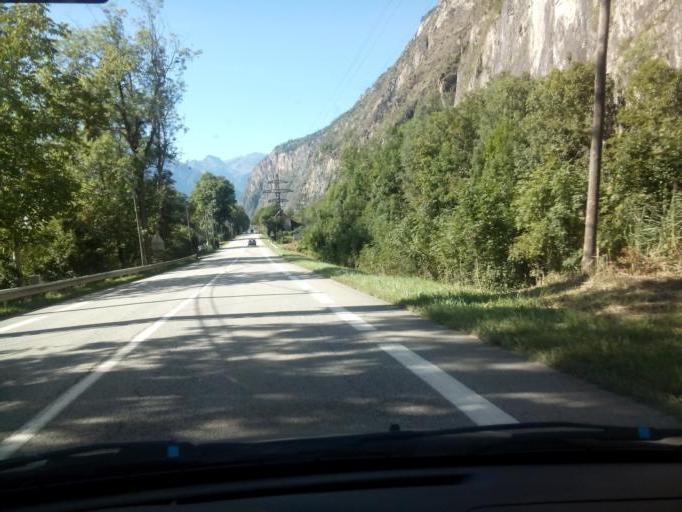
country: FR
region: Rhone-Alpes
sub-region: Departement de l'Isere
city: Huez
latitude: 45.0308
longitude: 6.0691
